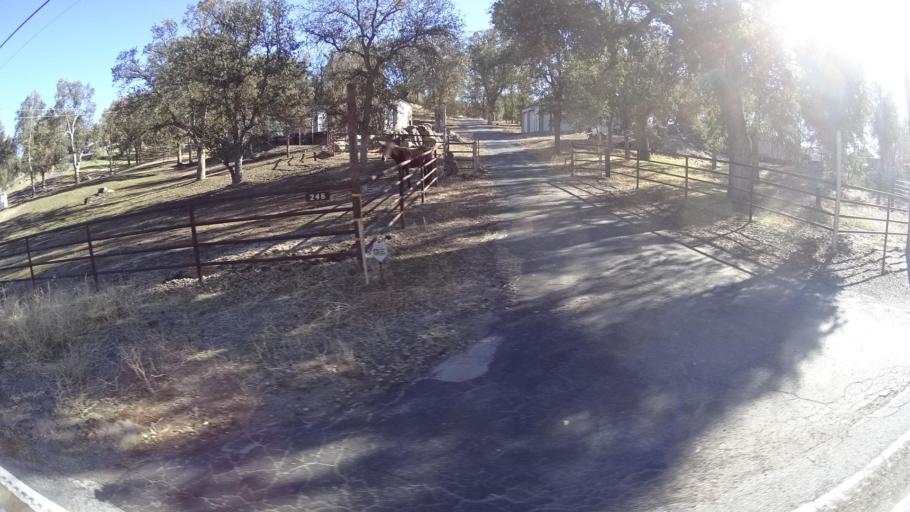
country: US
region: California
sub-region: Kern County
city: Alta Sierra
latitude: 35.7288
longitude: -118.7221
